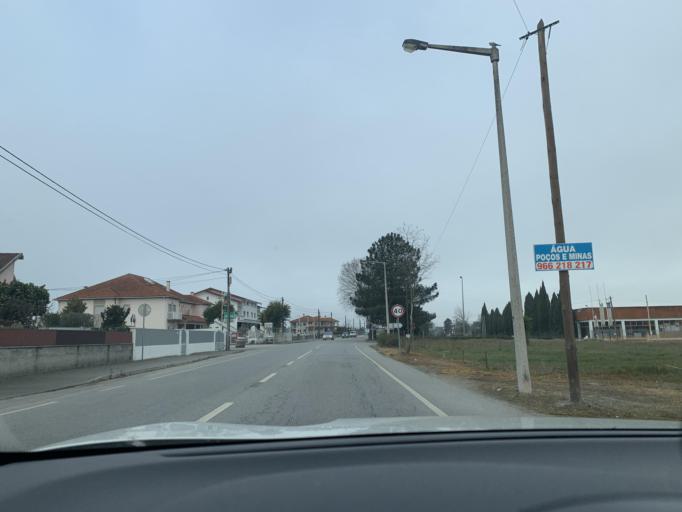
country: PT
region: Viseu
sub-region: Viseu
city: Rio de Loba
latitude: 40.6276
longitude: -7.8757
